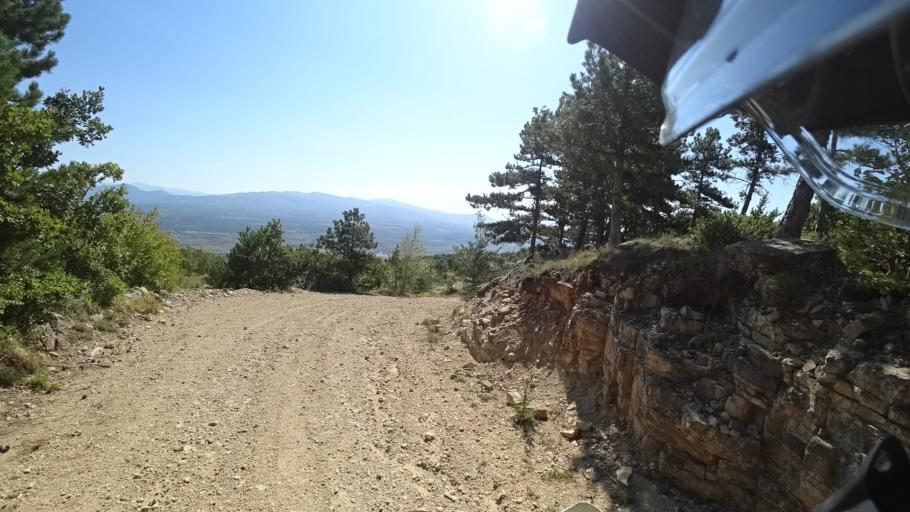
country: HR
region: Sibensko-Kniniska
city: Drnis
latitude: 43.8887
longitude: 16.1764
